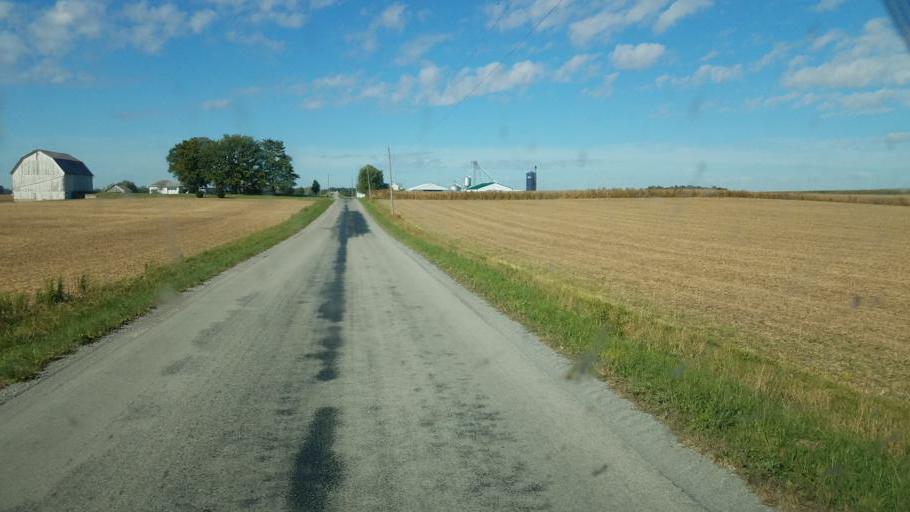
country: US
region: Ohio
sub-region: Wyandot County
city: Upper Sandusky
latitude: 40.8038
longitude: -83.2249
